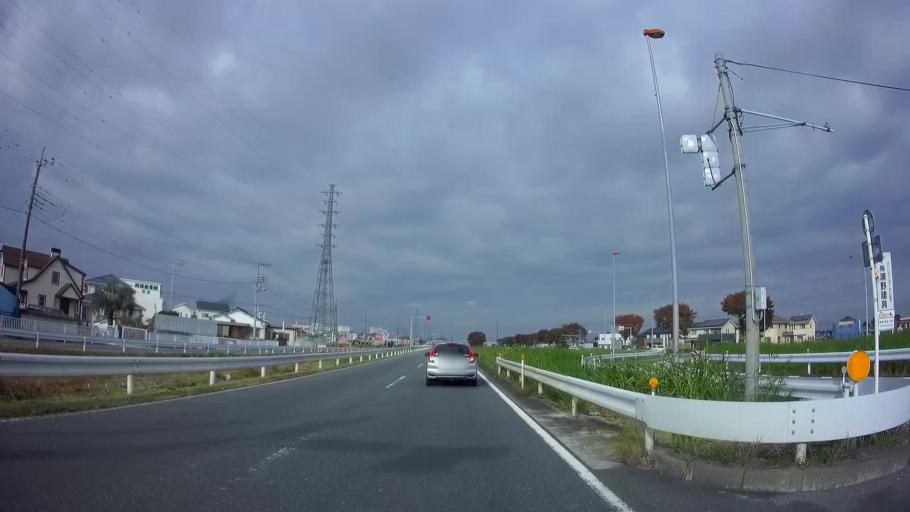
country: JP
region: Saitama
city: Gyoda
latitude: 36.1297
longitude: 139.4480
